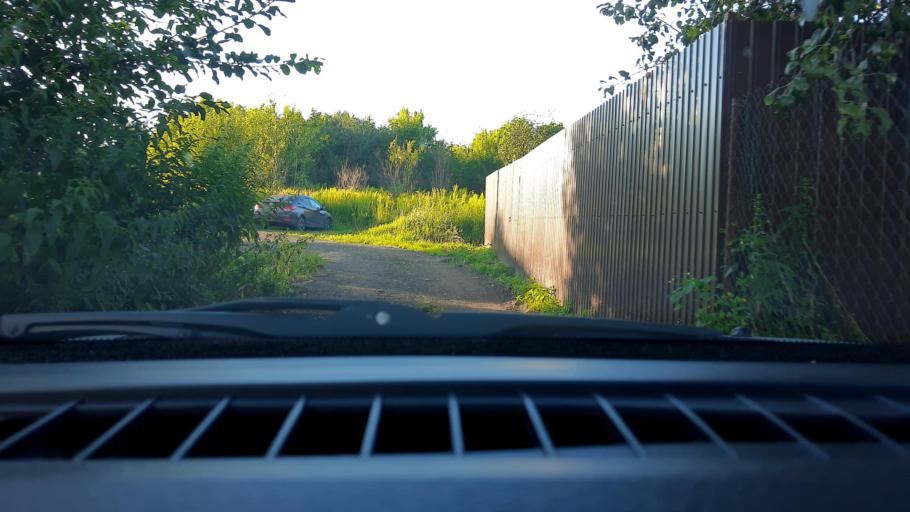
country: RU
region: Nizjnij Novgorod
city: Afonino
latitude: 56.2212
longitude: 44.1007
